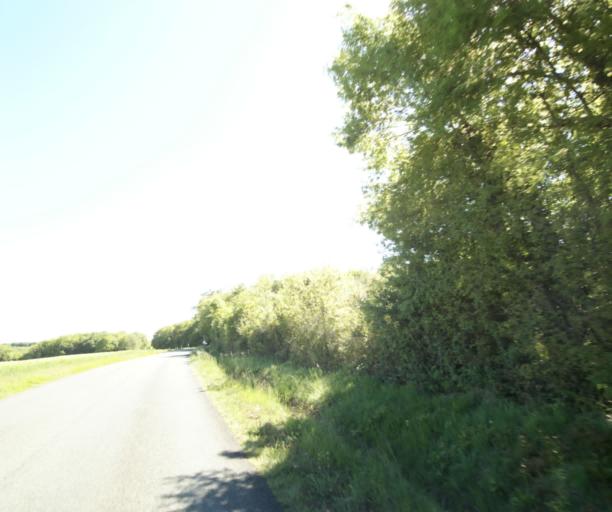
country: FR
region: Poitou-Charentes
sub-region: Departement de la Charente-Maritime
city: Bussac-sur-Charente
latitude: 45.8065
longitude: -0.6632
